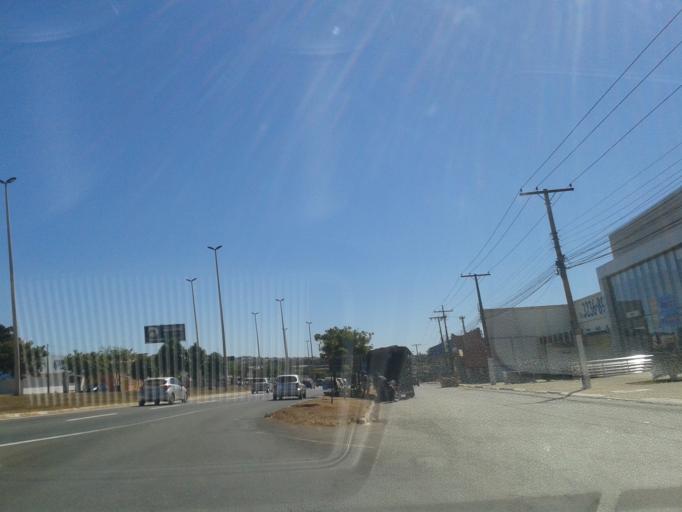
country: BR
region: Goias
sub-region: Goiania
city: Goiania
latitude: -16.6514
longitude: -49.3332
